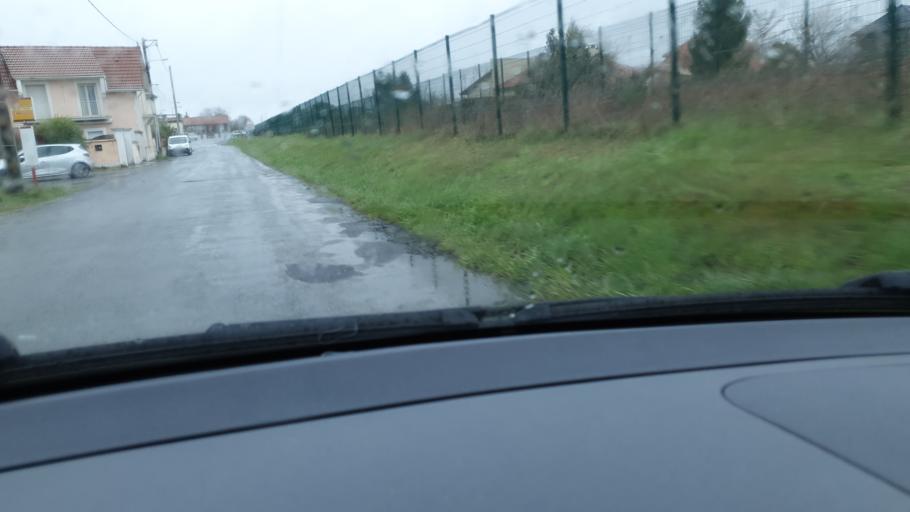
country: FR
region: Midi-Pyrenees
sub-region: Departement des Hautes-Pyrenees
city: Tarbes
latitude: 43.2508
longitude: 0.0538
